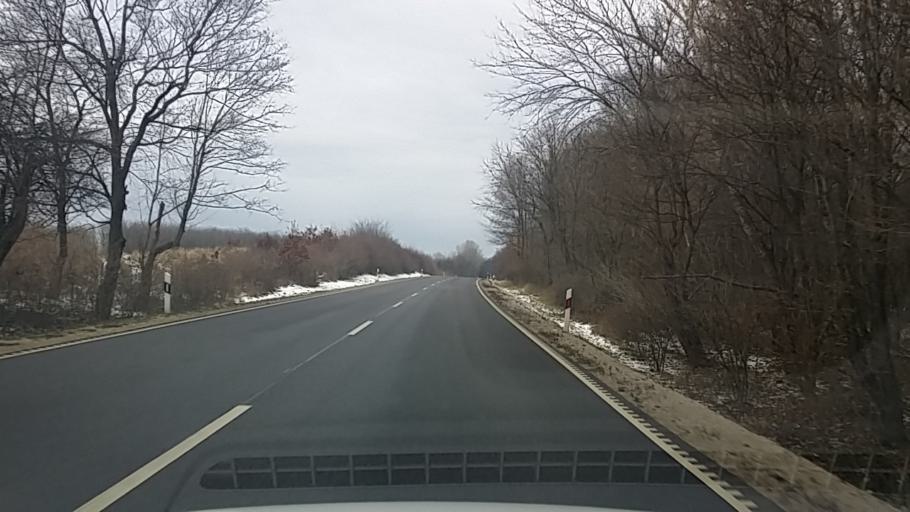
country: HU
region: Komarom-Esztergom
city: Csaszar
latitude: 47.4581
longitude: 18.0949
